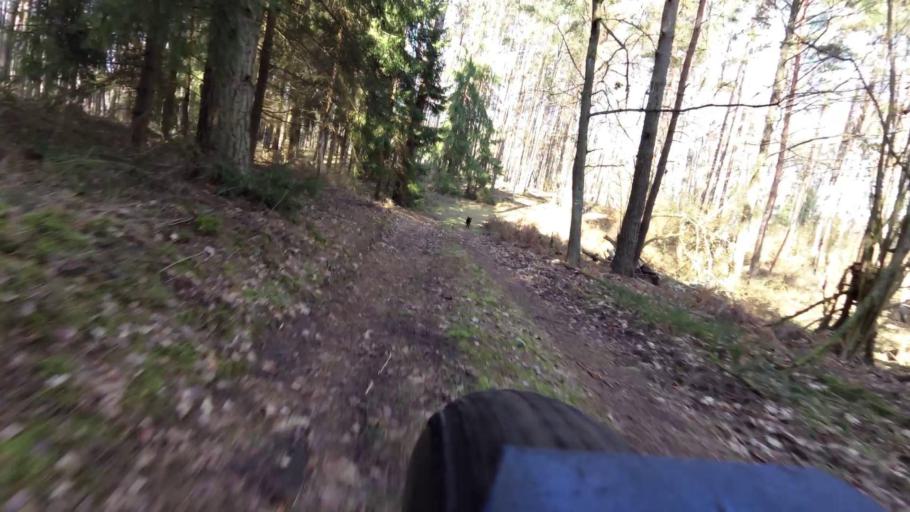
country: PL
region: Lubusz
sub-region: Powiat sulecinski
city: Torzym
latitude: 52.2195
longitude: 14.9698
